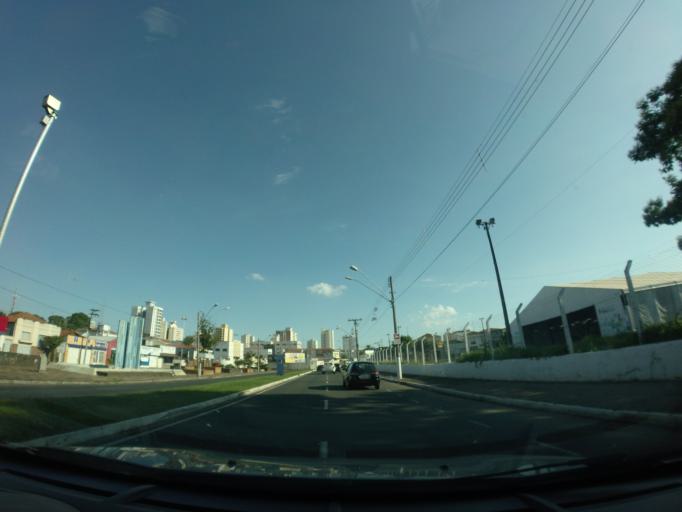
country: BR
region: Sao Paulo
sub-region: Rio Claro
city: Rio Claro
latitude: -22.4058
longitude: -47.5649
